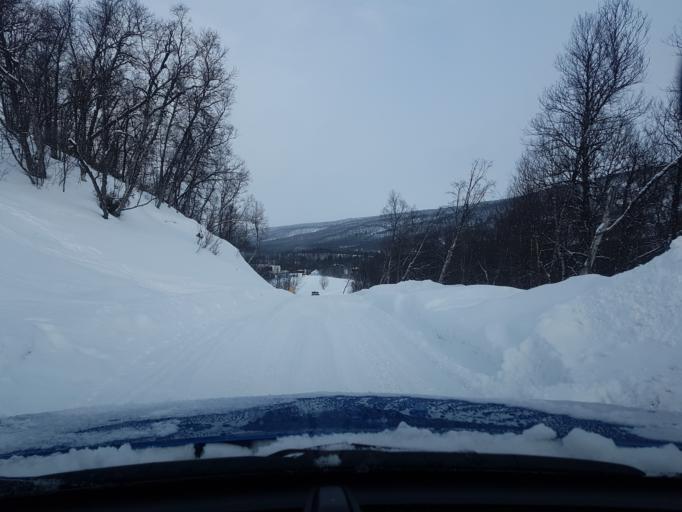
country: NO
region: Sor-Trondelag
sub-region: Tydal
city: Aas
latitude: 62.6926
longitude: 12.3988
